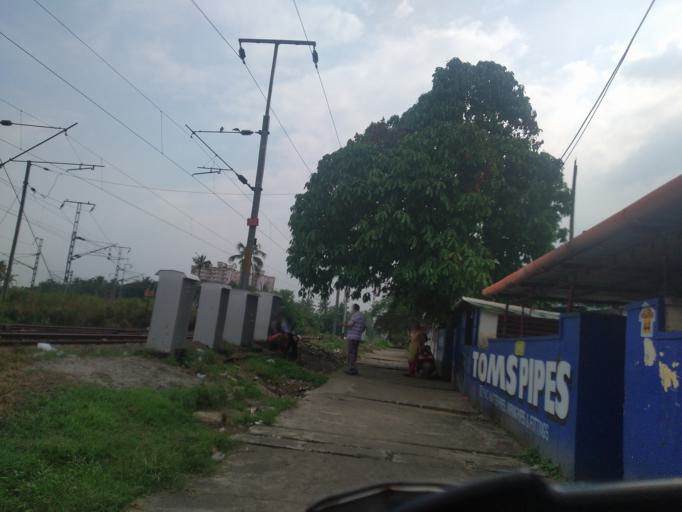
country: IN
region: Kerala
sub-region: Ernakulam
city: Cochin
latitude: 9.9817
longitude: 76.2885
